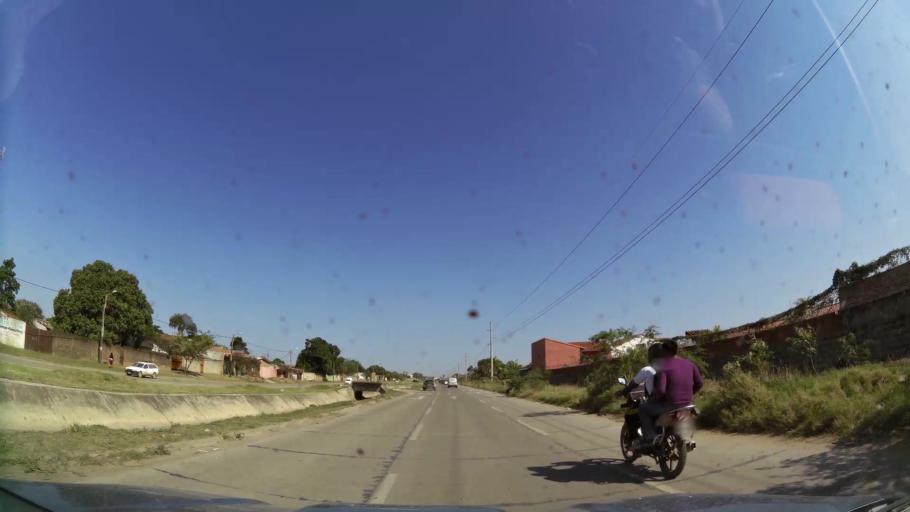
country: BO
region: Santa Cruz
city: Santa Cruz de la Sierra
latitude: -17.7677
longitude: -63.1079
